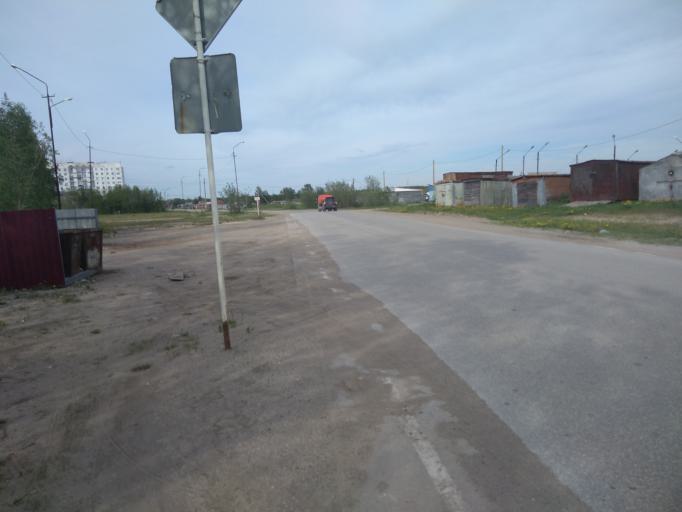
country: RU
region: Komi Republic
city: Pechora
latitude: 65.1437
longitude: 57.2347
